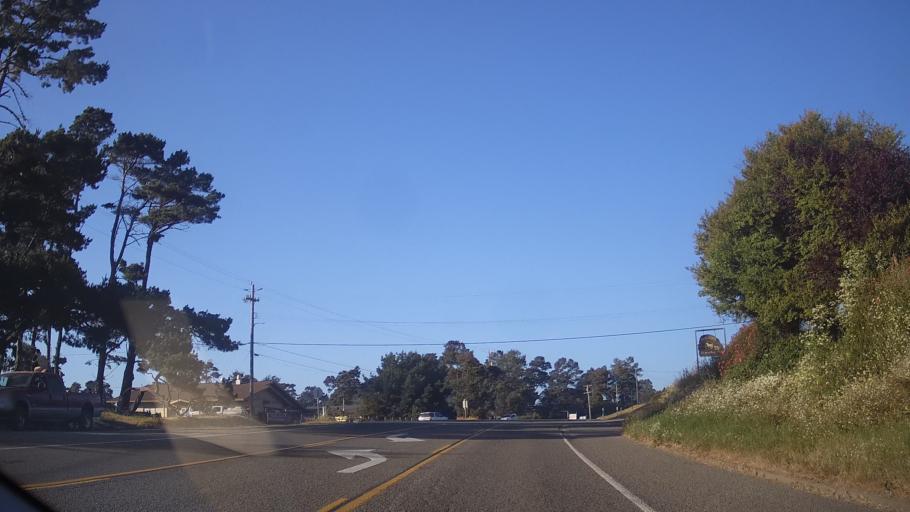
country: US
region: California
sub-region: Mendocino County
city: Fort Bragg
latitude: 39.4895
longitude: -123.7864
